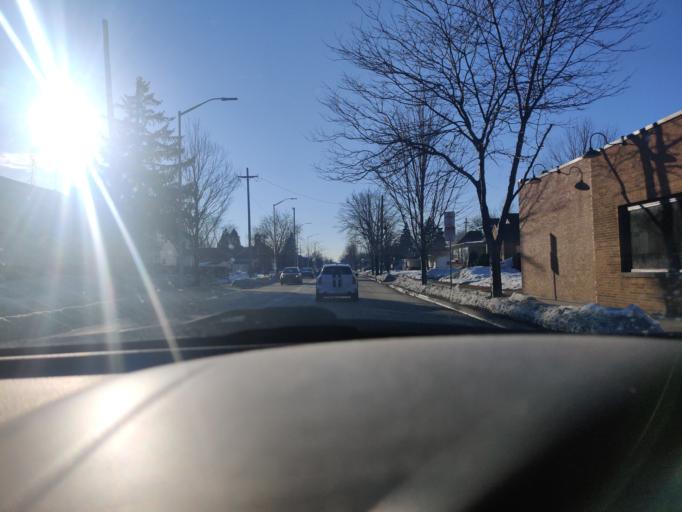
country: US
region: Wisconsin
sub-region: Kenosha County
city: Kenosha
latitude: 42.5659
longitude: -87.8366
